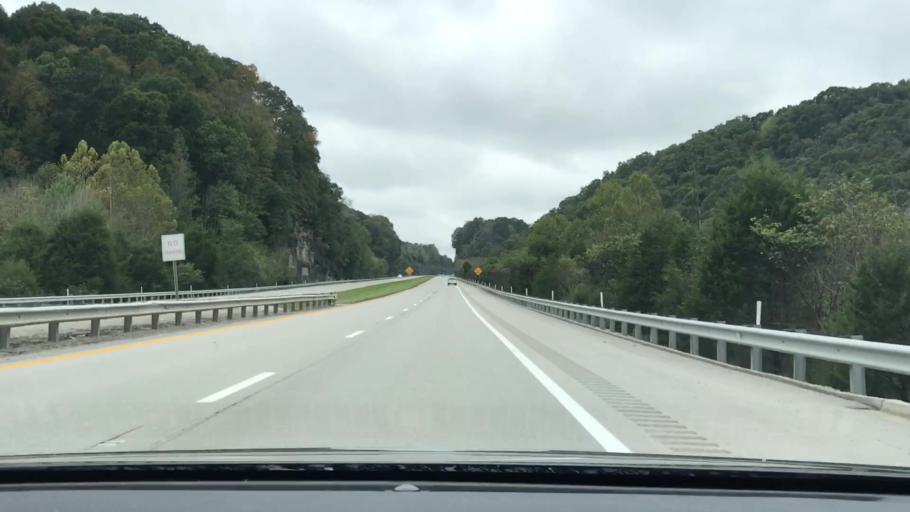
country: US
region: Kentucky
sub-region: Pulaski County
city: Somerset
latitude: 37.0971
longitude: -84.6962
